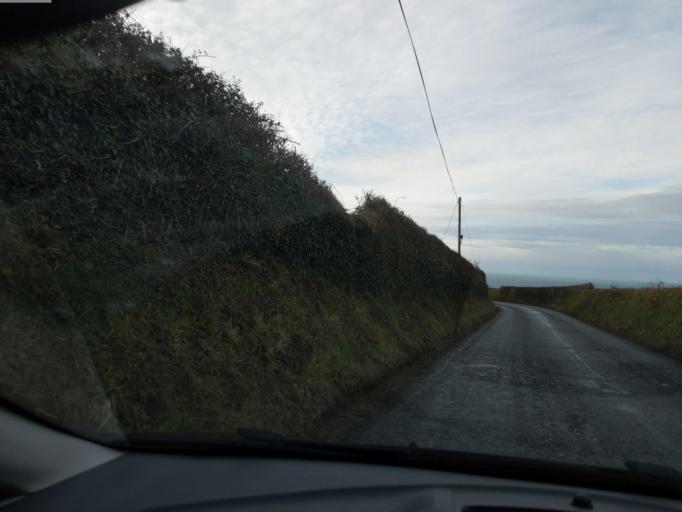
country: GB
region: England
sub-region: Cornwall
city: Camelford
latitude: 50.6946
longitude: -4.6743
